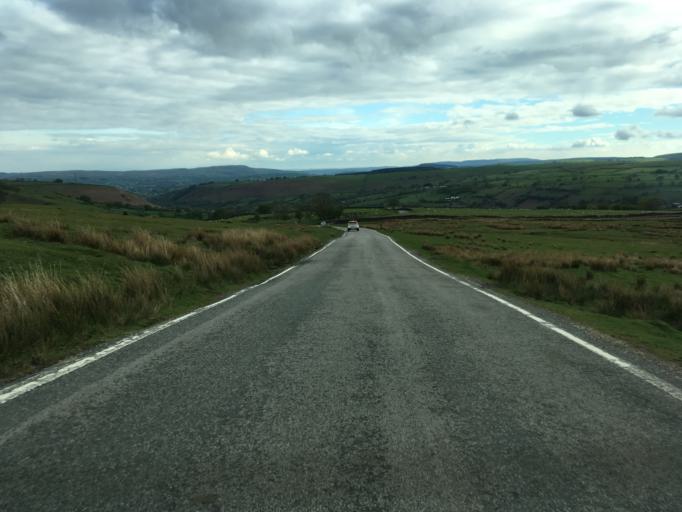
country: GB
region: Wales
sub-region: Caerphilly County Borough
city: Rhymney
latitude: 51.7156
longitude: -3.3080
